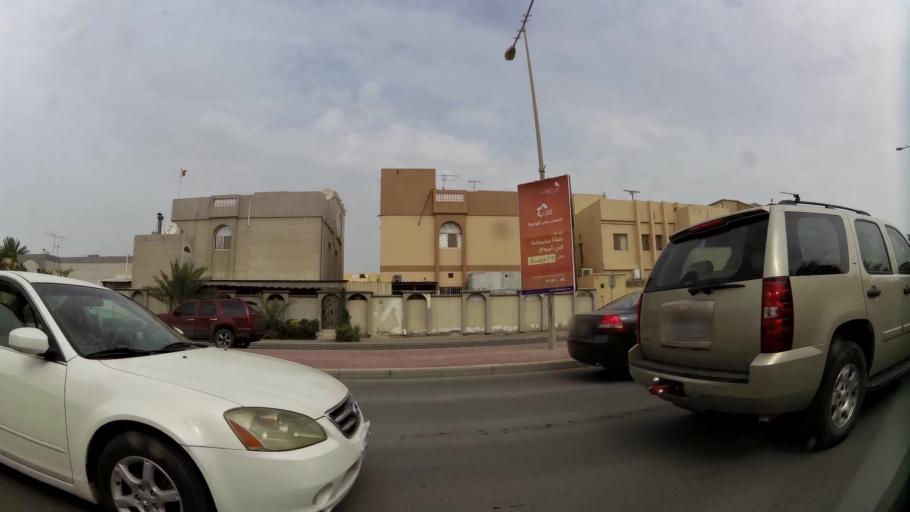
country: BH
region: Northern
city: Ar Rifa'
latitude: 26.1302
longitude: 50.5625
